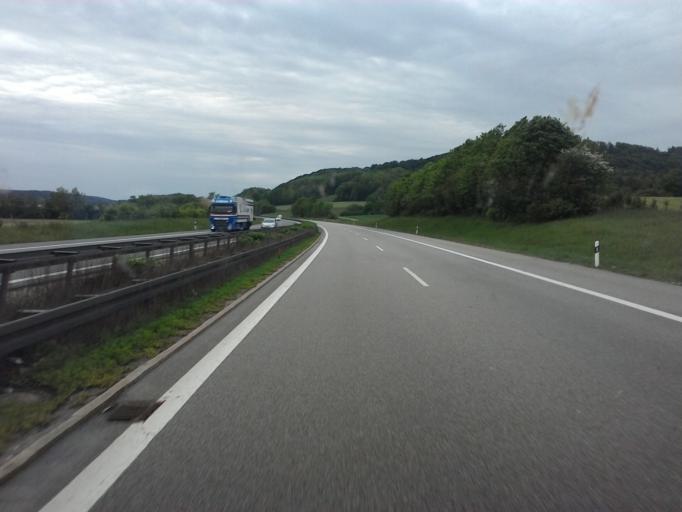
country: DE
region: Bavaria
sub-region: Upper Palatinate
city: Pilsach
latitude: 49.3385
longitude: 11.4520
